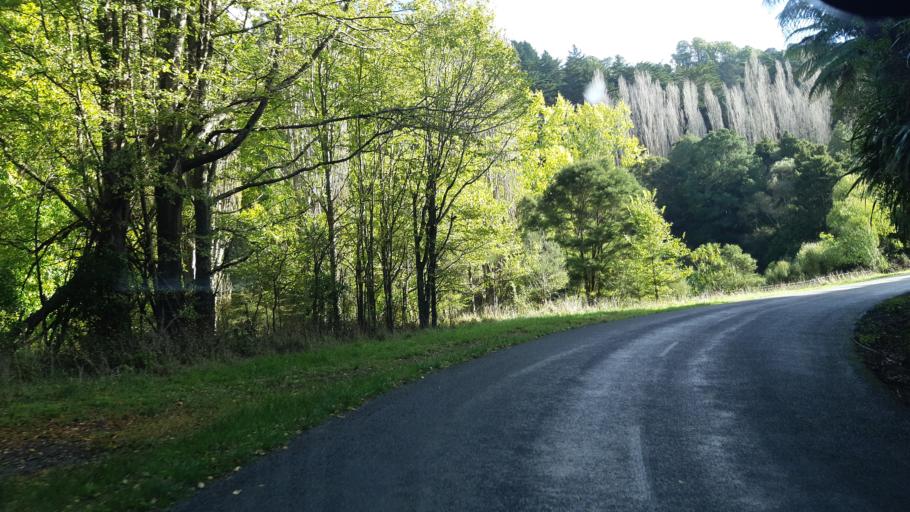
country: NZ
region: Manawatu-Wanganui
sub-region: Wanganui District
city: Wanganui
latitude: -39.9401
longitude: 175.2568
